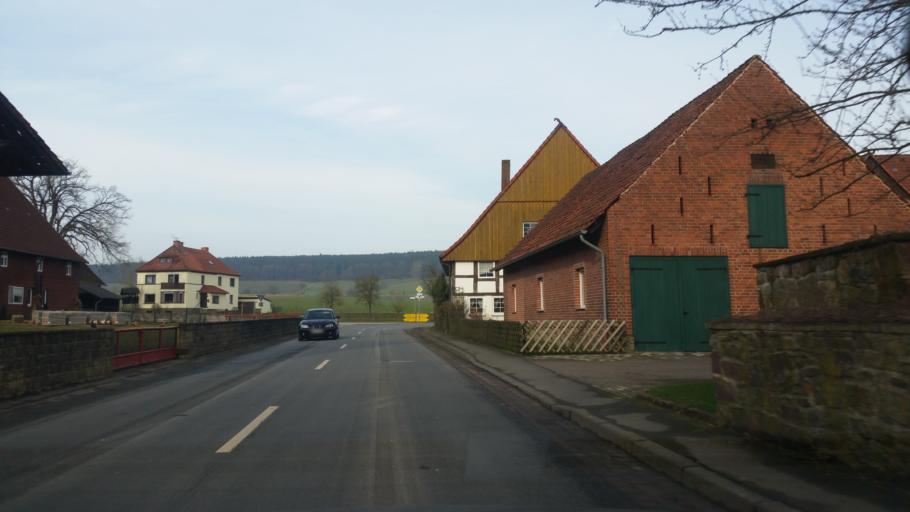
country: DE
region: Lower Saxony
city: Aerzen
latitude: 52.0737
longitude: 9.2242
